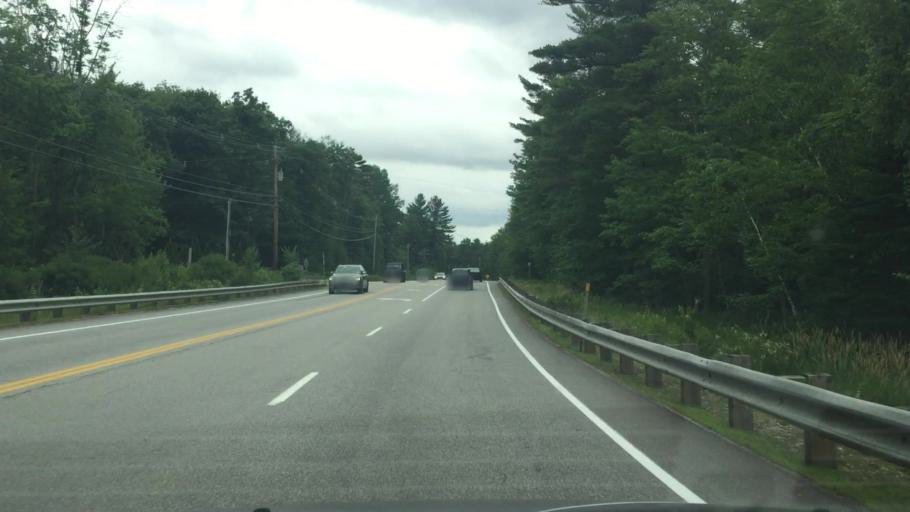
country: US
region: New Hampshire
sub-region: Carroll County
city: Center Harbor
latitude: 43.6817
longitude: -71.4670
